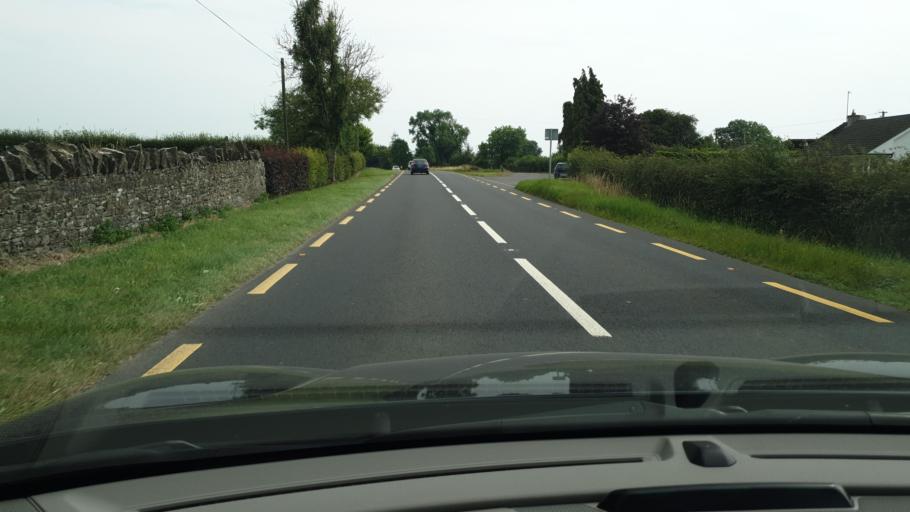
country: IE
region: Leinster
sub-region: An Mhi
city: Kells
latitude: 53.6992
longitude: -6.9363
